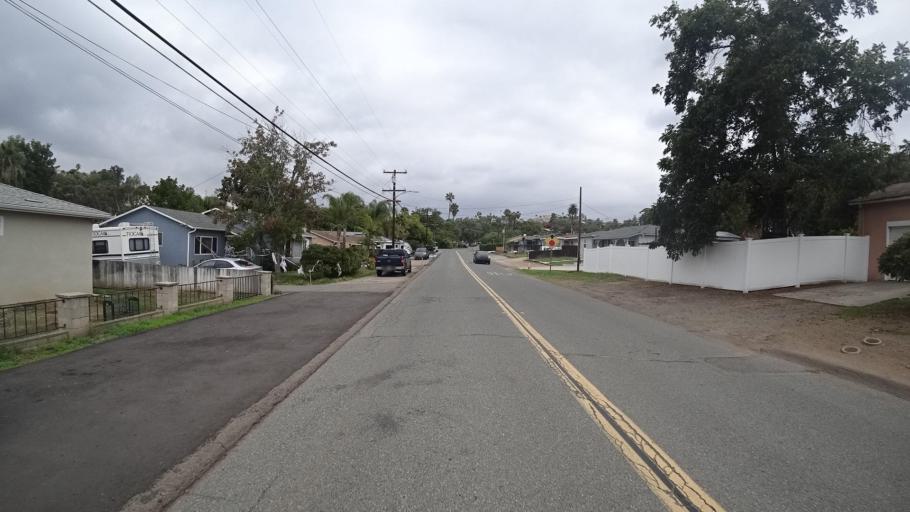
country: US
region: California
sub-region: San Diego County
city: Spring Valley
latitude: 32.7537
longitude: -116.9993
